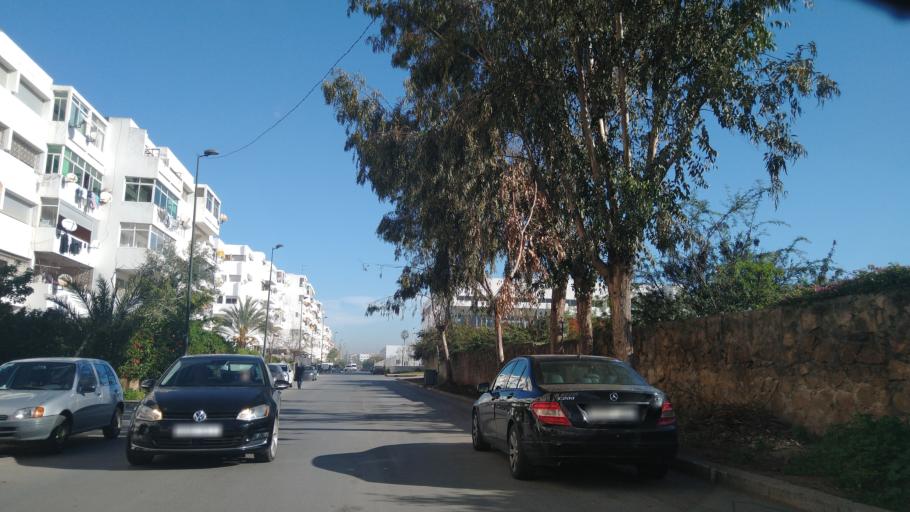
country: MA
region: Rabat-Sale-Zemmour-Zaer
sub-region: Rabat
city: Rabat
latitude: 33.9907
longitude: -6.8816
